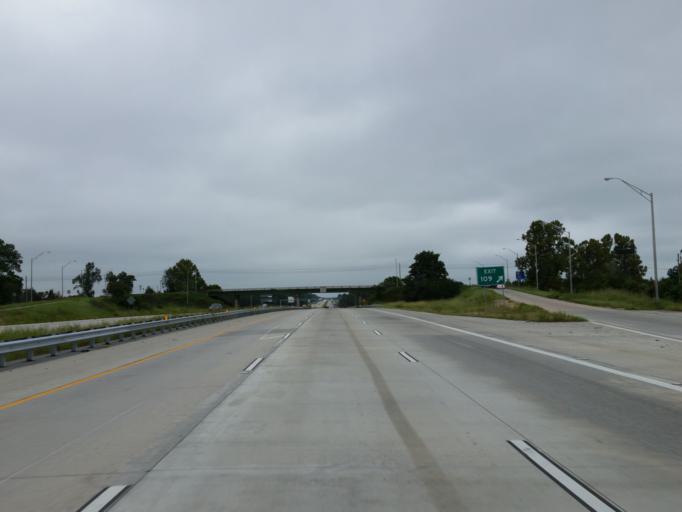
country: US
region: Georgia
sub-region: Dooly County
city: Vienna
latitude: 32.0890
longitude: -83.7633
